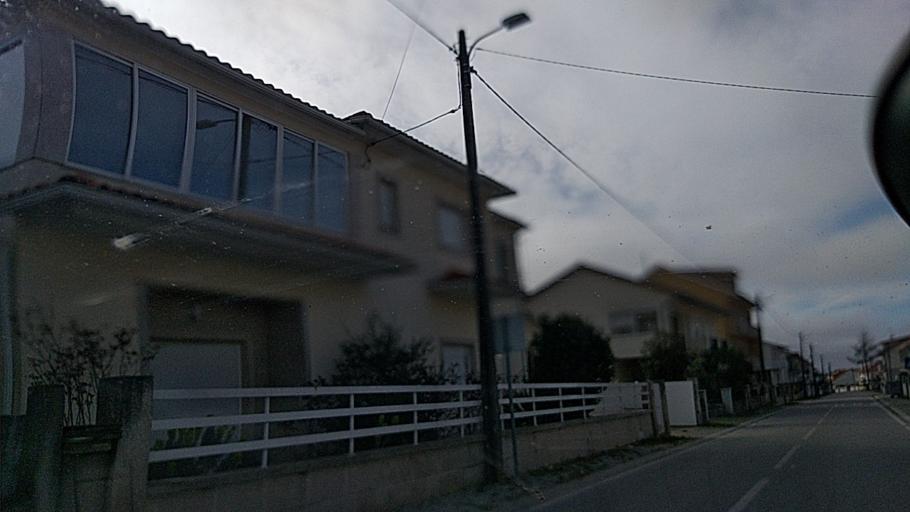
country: PT
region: Guarda
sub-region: Aguiar da Beira
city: Aguiar da Beira
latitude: 40.7826
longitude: -7.5176
